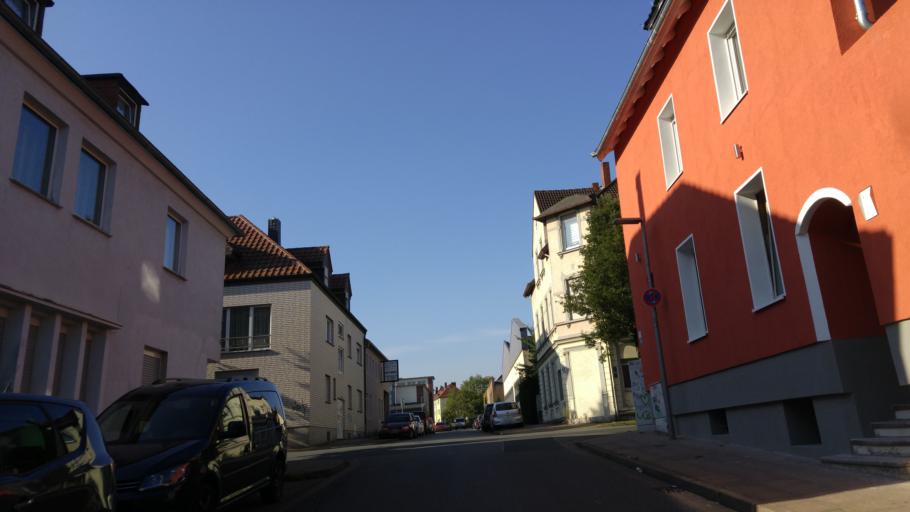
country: DE
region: North Rhine-Westphalia
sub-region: Regierungsbezirk Detmold
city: Bielefeld
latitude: 52.0328
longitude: 8.5300
